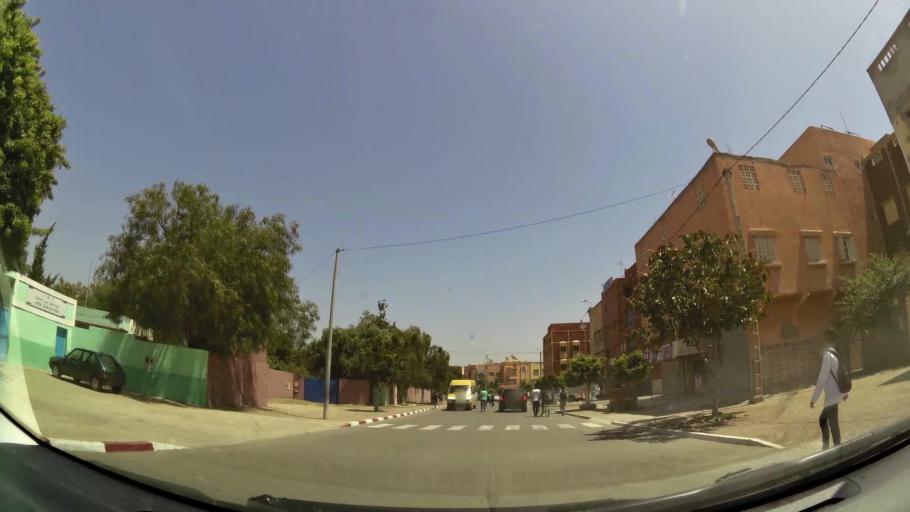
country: MA
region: Souss-Massa-Draa
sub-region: Inezgane-Ait Mellou
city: Inezgane
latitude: 30.3473
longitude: -9.4863
